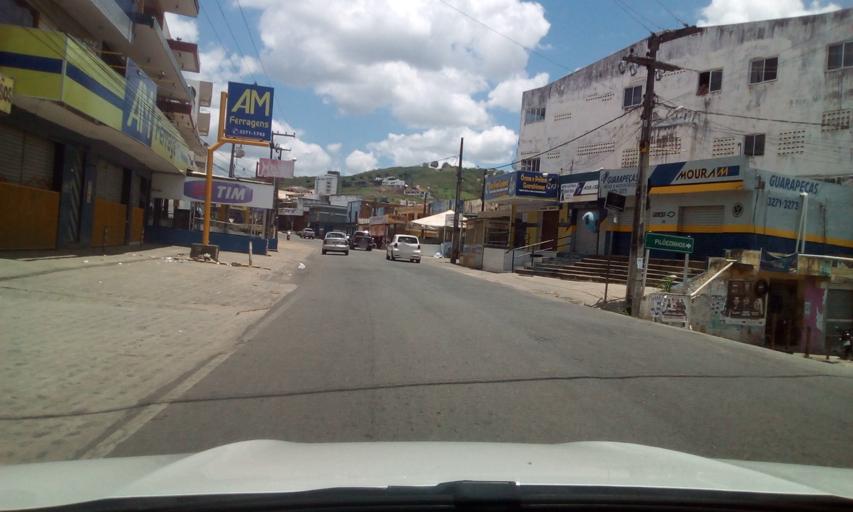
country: BR
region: Paraiba
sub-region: Guarabira
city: Guarabira
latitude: -6.8521
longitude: -35.4942
